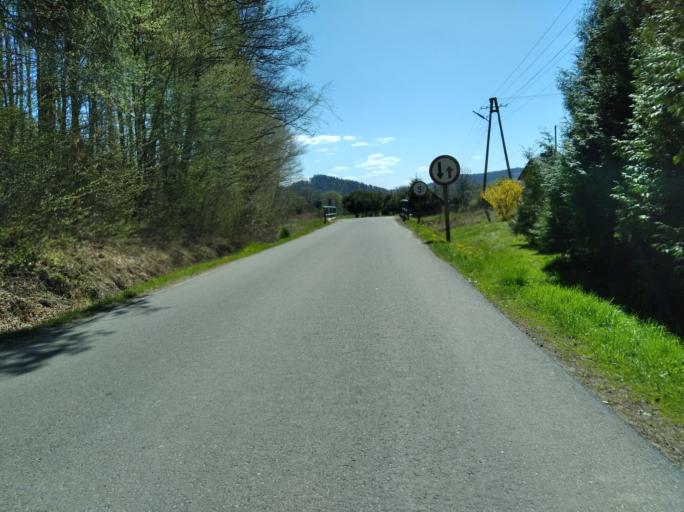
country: PL
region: Subcarpathian Voivodeship
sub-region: Powiat brzozowski
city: Dydnia
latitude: 49.7118
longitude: 22.1991
